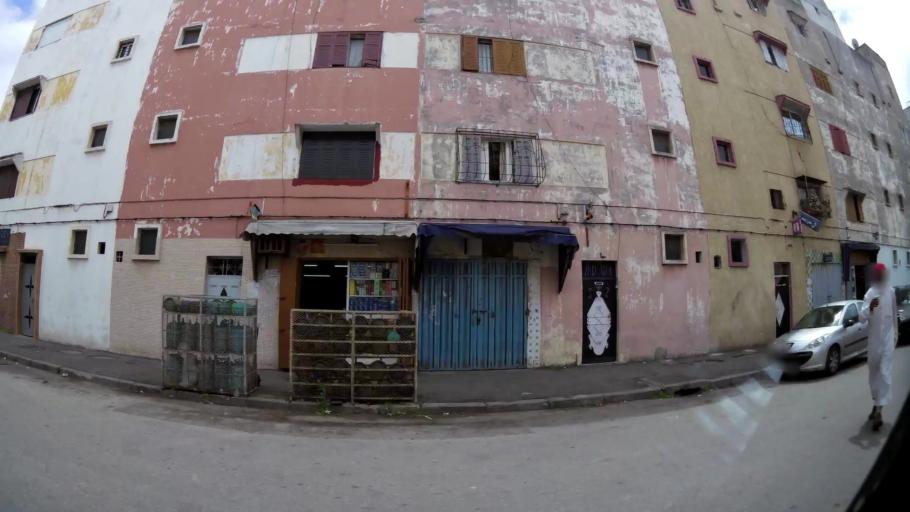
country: MA
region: Grand Casablanca
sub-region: Casablanca
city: Casablanca
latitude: 33.5767
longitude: -7.5624
